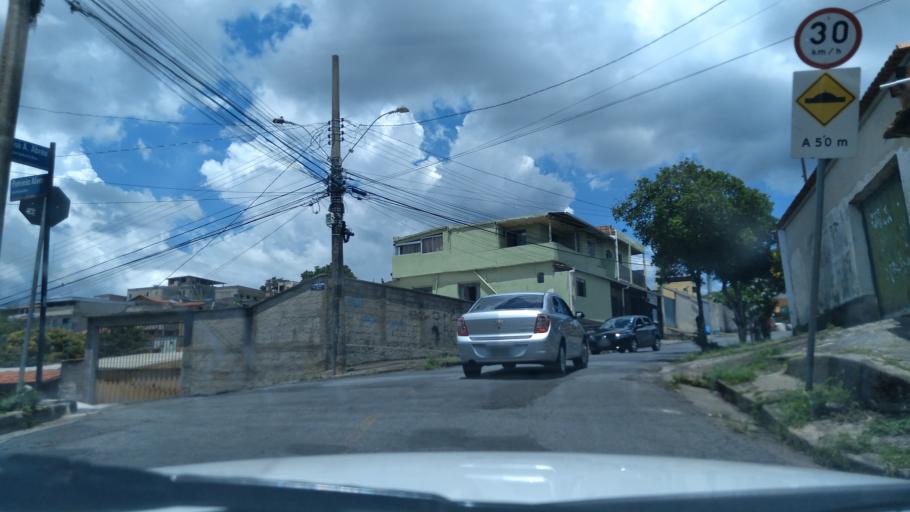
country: BR
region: Minas Gerais
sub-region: Belo Horizonte
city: Belo Horizonte
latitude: -19.8686
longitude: -43.9015
